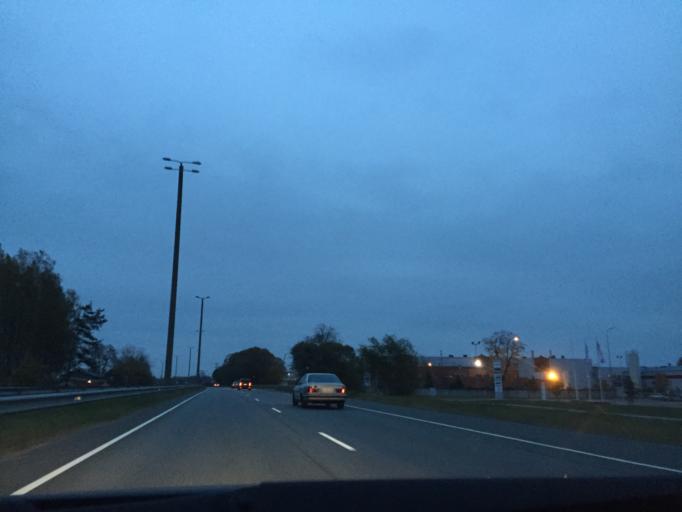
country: LV
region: Marupe
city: Marupe
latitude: 56.8855
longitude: 24.0743
